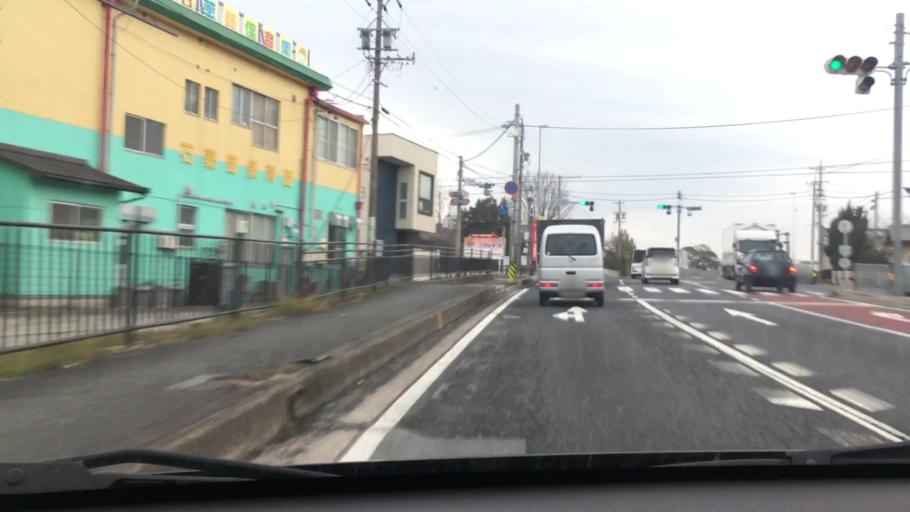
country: JP
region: Mie
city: Suzuka
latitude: 34.9022
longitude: 136.5486
